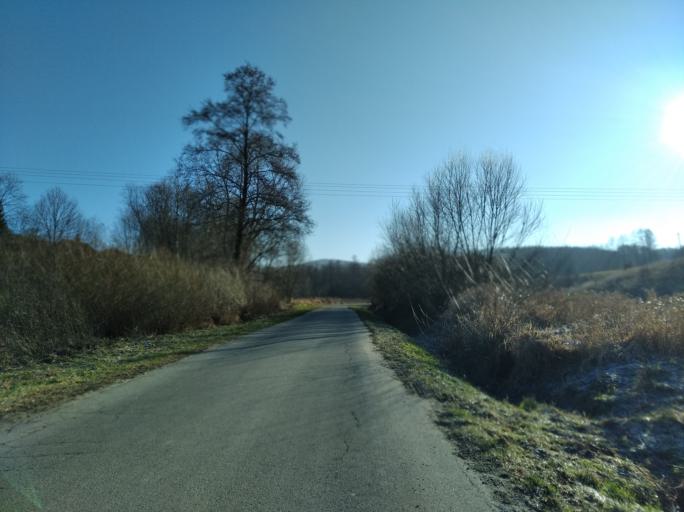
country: PL
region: Subcarpathian Voivodeship
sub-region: Powiat strzyzowski
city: Wysoka Strzyzowska
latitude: 49.8491
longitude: 21.7610
